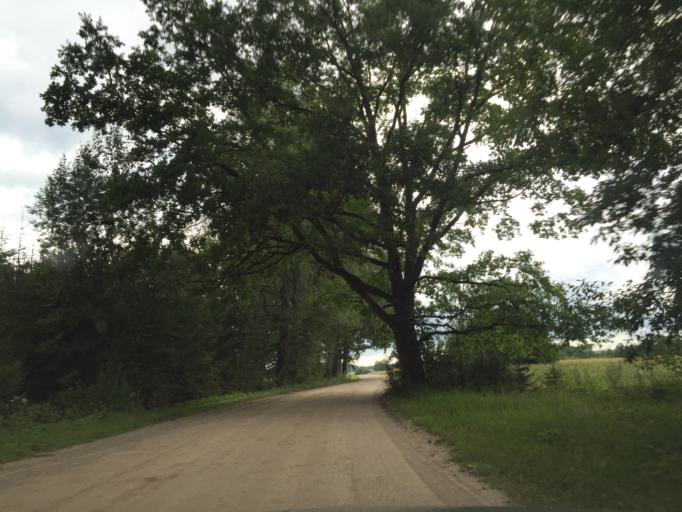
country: LV
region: Malpils
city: Malpils
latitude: 56.9472
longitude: 24.9976
